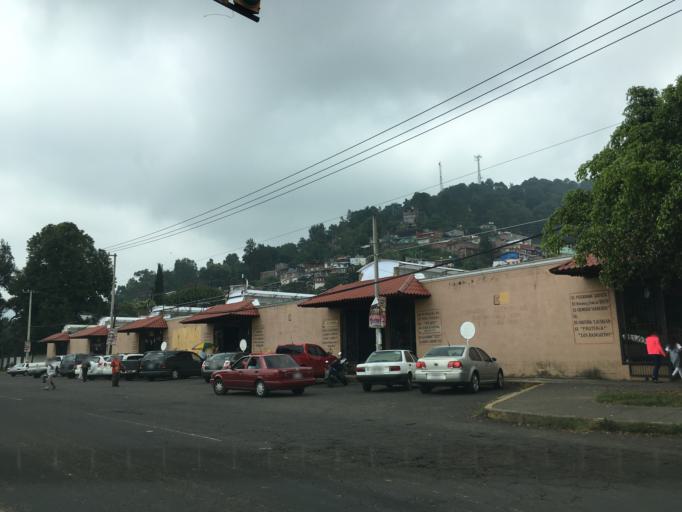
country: MX
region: Michoacan
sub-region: Uruapan
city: Uruapan
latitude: 19.4278
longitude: -102.0594
